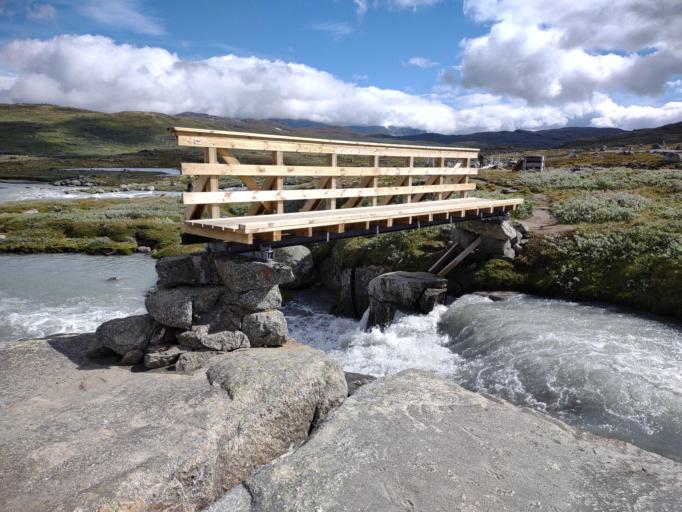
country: NO
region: Hordaland
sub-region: Eidfjord
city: Eidfjord
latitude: 60.5841
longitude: 7.5193
